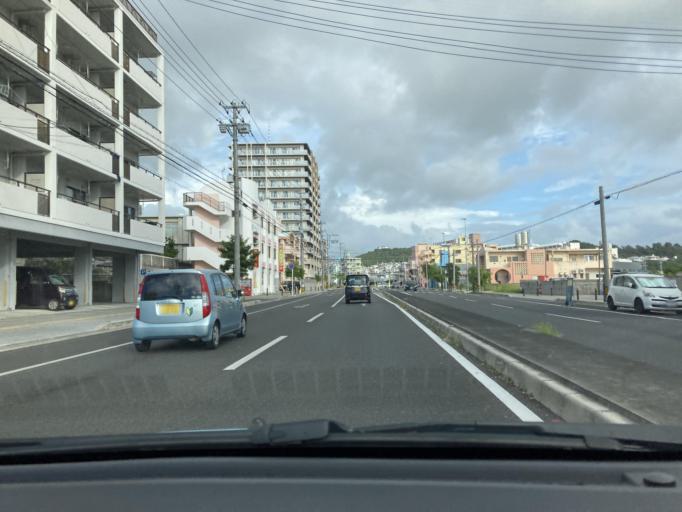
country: JP
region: Okinawa
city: Tomigusuku
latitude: 26.1775
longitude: 127.6727
